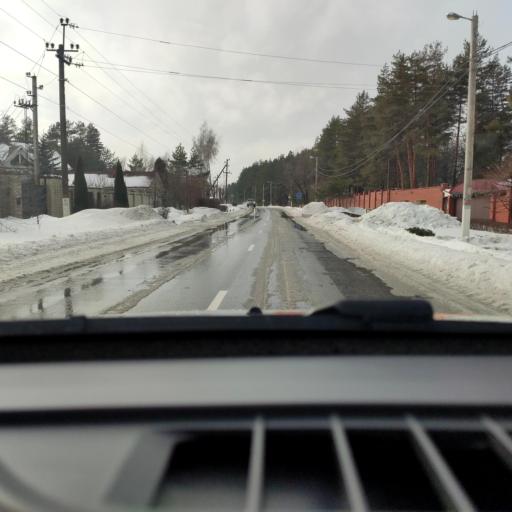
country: RU
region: Voronezj
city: Podgornoye
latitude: 51.7837
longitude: 39.1409
